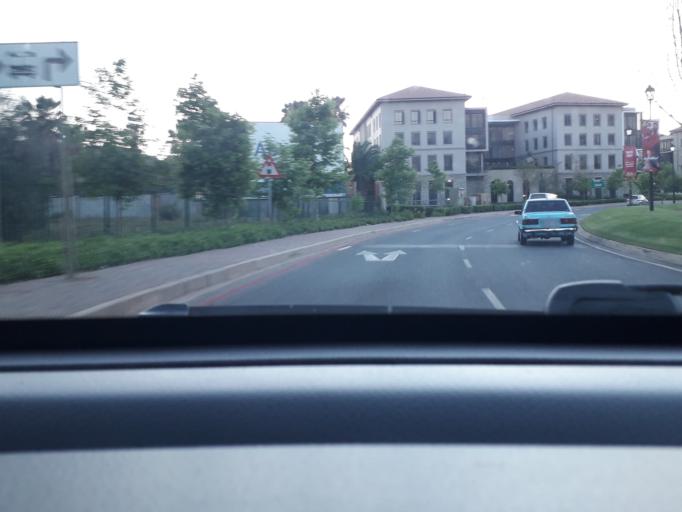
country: ZA
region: Gauteng
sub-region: City of Johannesburg Metropolitan Municipality
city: Diepsloot
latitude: -26.0265
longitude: 28.0155
